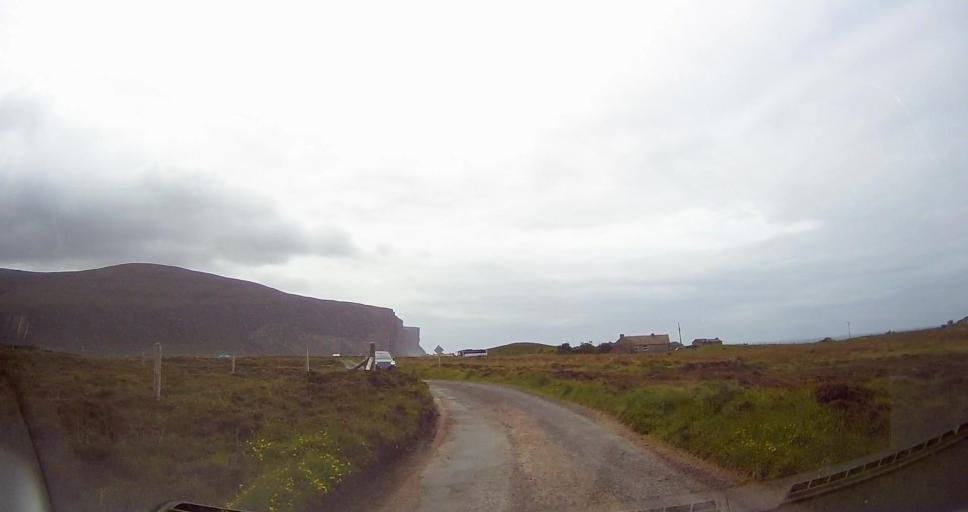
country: GB
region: Scotland
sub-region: Orkney Islands
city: Stromness
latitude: 58.8753
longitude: -3.3867
